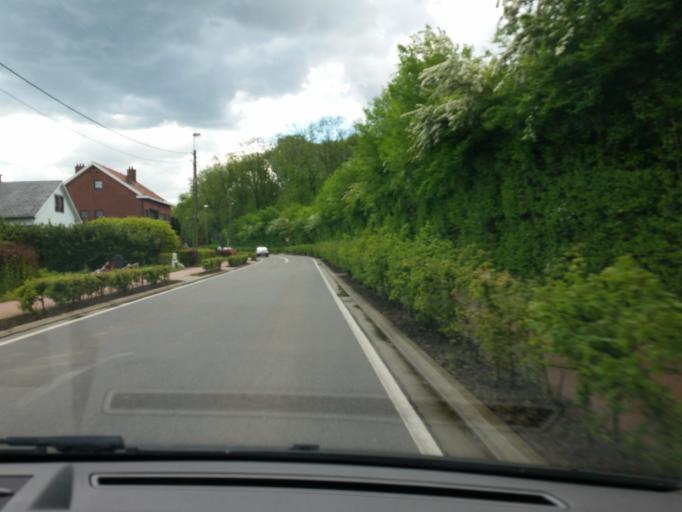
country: BE
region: Flanders
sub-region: Provincie Vlaams-Brabant
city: Zemst
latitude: 50.9606
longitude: 4.4706
